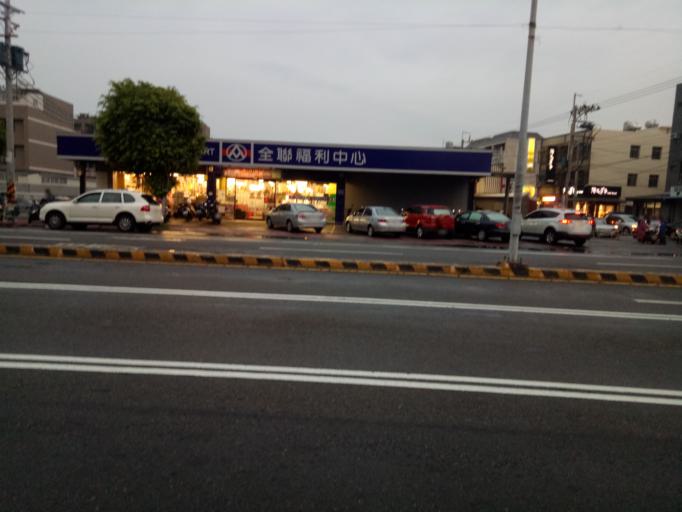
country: TW
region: Taiwan
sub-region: Changhua
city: Chang-hua
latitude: 24.2454
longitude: 120.5378
